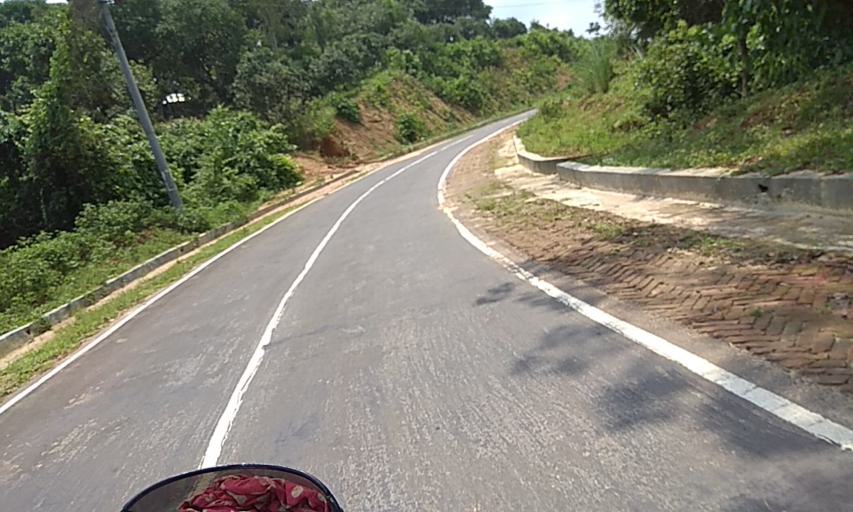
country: BD
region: Chittagong
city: Manikchari
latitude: 22.9387
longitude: 91.9030
